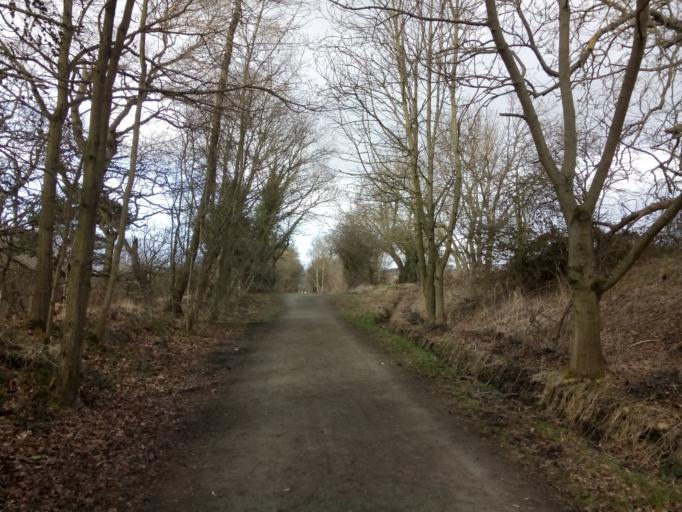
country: GB
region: England
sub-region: County Durham
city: Ushaw Moor
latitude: 54.7715
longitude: -1.6350
